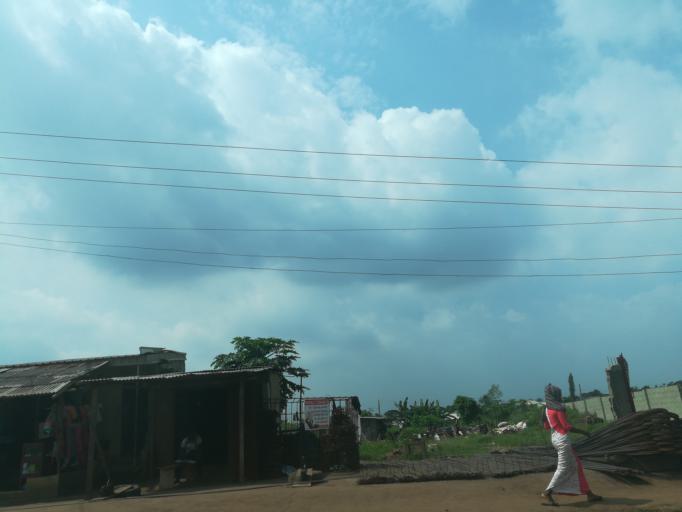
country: NG
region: Lagos
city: Ikorodu
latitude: 6.6008
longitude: 3.6259
